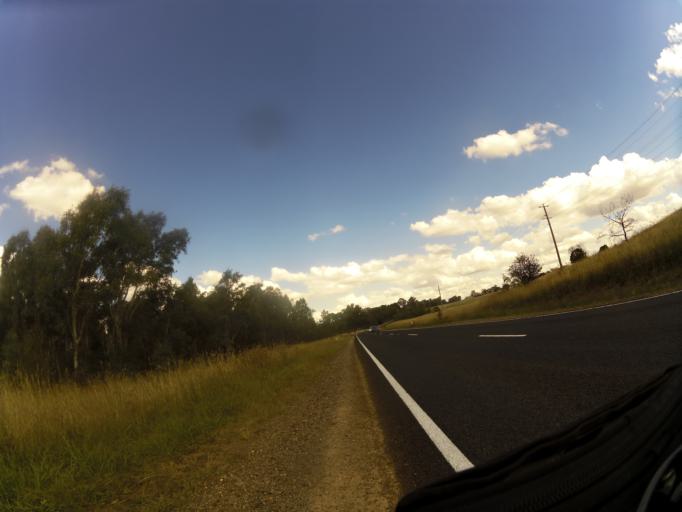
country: AU
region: Victoria
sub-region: Mansfield
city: Mansfield
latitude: -36.9086
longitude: 145.9987
